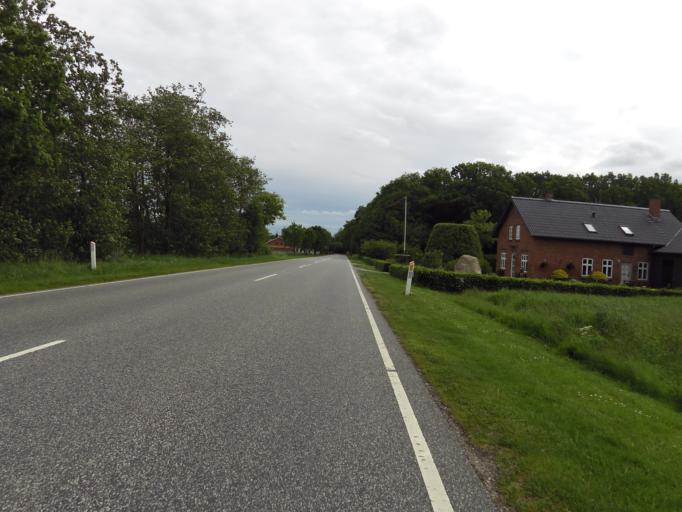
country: DK
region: South Denmark
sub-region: Haderslev Kommune
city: Gram
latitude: 55.3160
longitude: 9.0642
